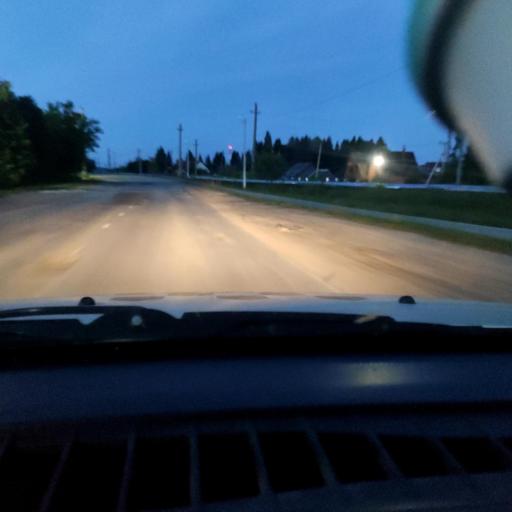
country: RU
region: Perm
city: Polazna
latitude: 58.2922
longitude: 56.4021
